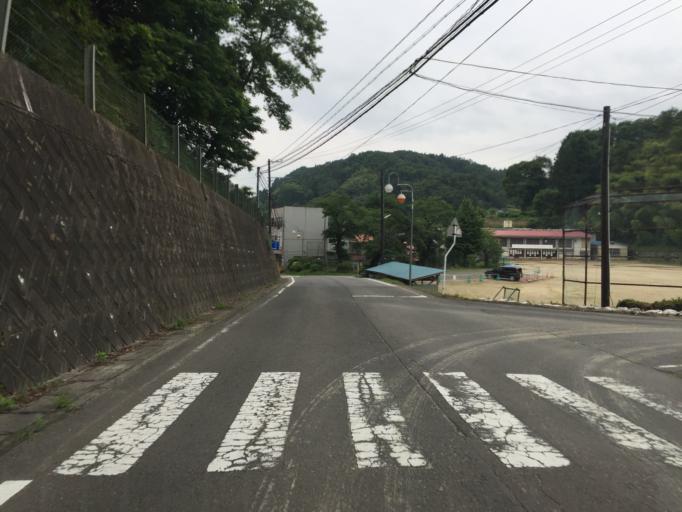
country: JP
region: Fukushima
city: Nihommatsu
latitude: 37.6197
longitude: 140.5581
